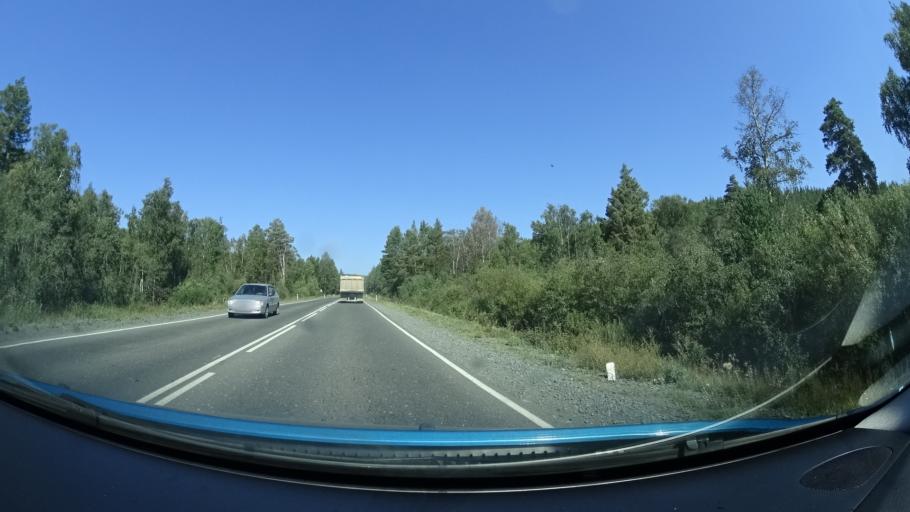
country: RU
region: Bashkortostan
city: Abzakovo
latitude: 53.8645
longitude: 58.5427
